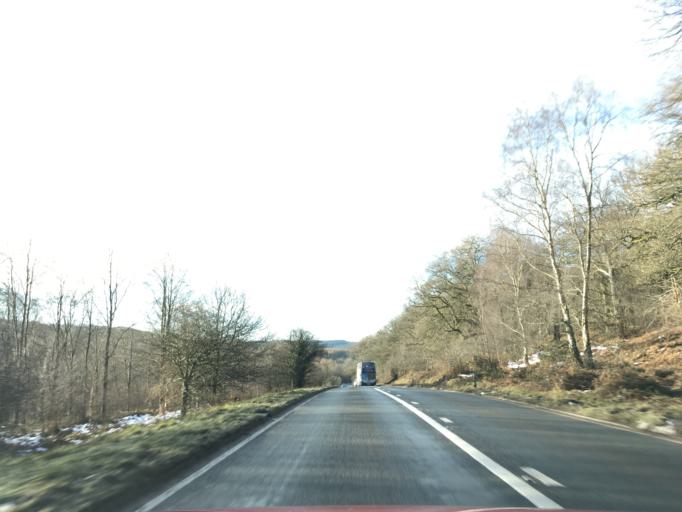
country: GB
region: England
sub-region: Gloucestershire
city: Ruardean
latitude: 51.8359
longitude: -2.5360
